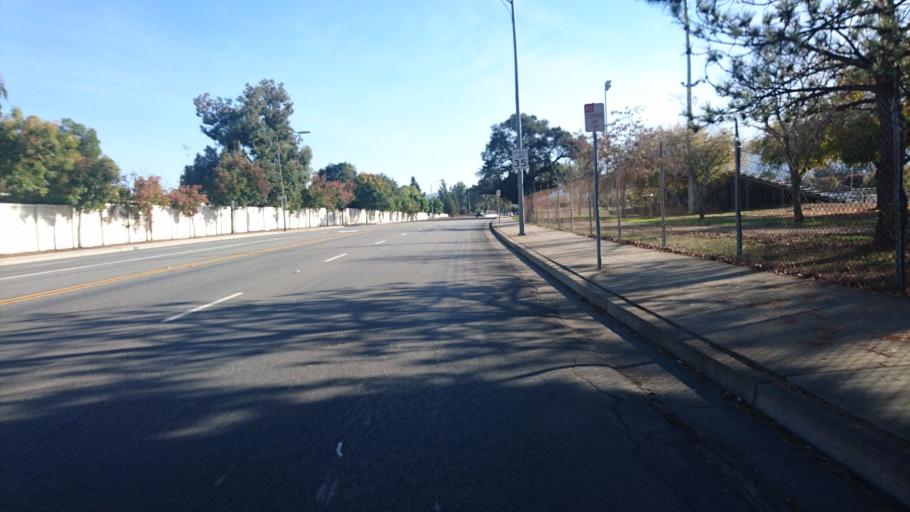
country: US
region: California
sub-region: Santa Clara County
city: Cambrian Park
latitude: 37.2532
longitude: -121.8967
